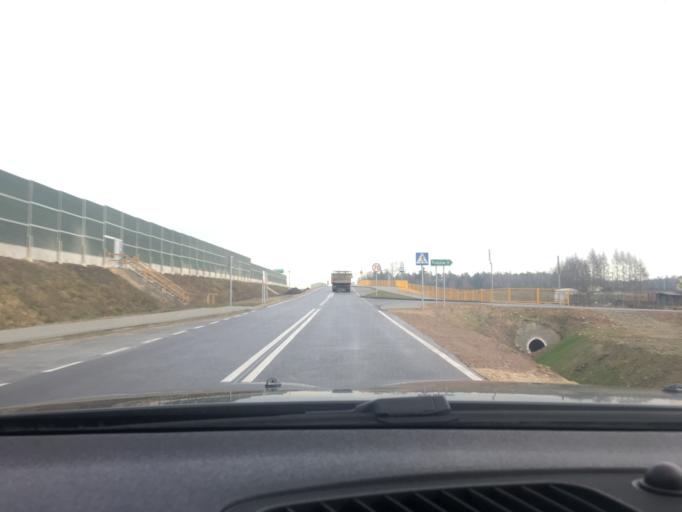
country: PL
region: Swietokrzyskie
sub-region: Powiat jedrzejowski
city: Jedrzejow
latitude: 50.6674
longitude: 20.3399
